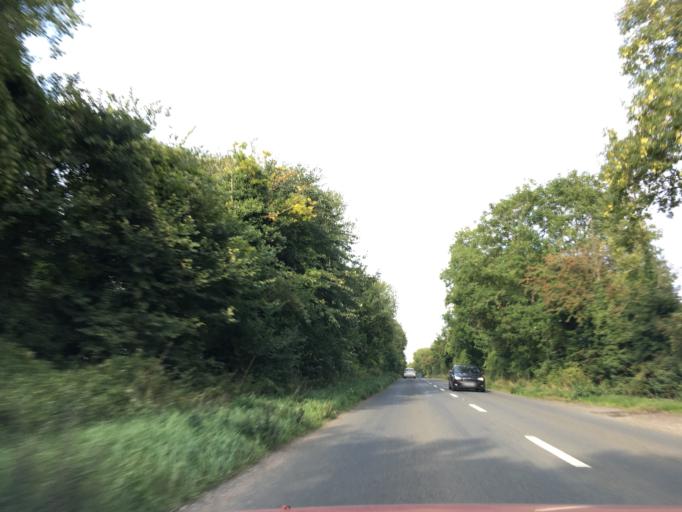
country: GB
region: England
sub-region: Gloucestershire
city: Coates
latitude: 51.6786
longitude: -2.0443
